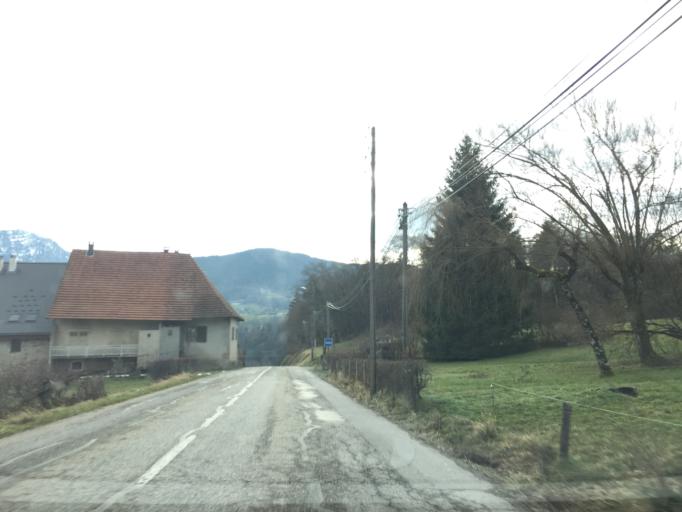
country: FR
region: Rhone-Alpes
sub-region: Departement de la Haute-Savoie
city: Gruffy
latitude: 45.7247
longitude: 6.1052
